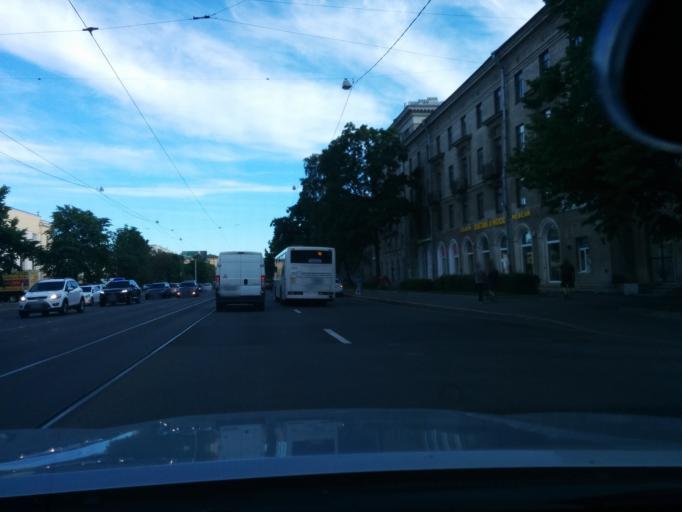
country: RU
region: Leningrad
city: Svetlanovskiy
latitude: 60.0088
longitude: 30.3255
